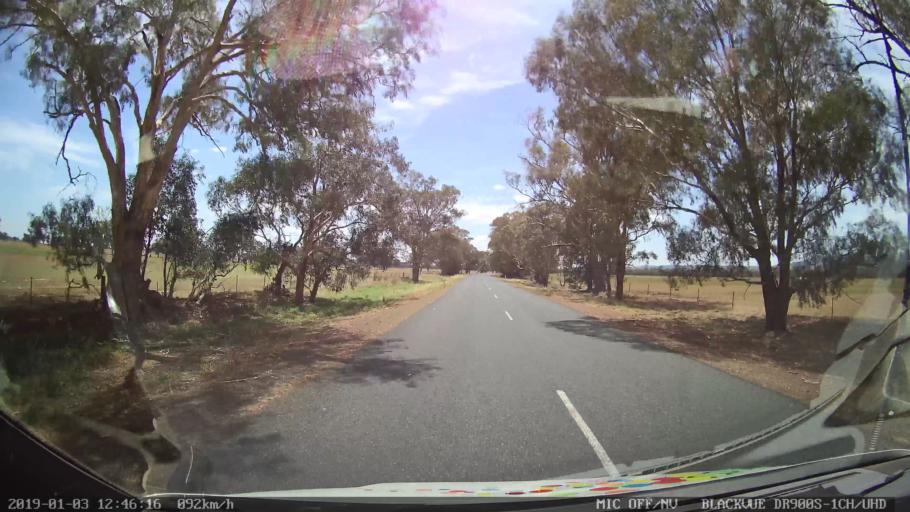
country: AU
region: New South Wales
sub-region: Weddin
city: Grenfell
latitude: -33.7400
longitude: 148.2313
